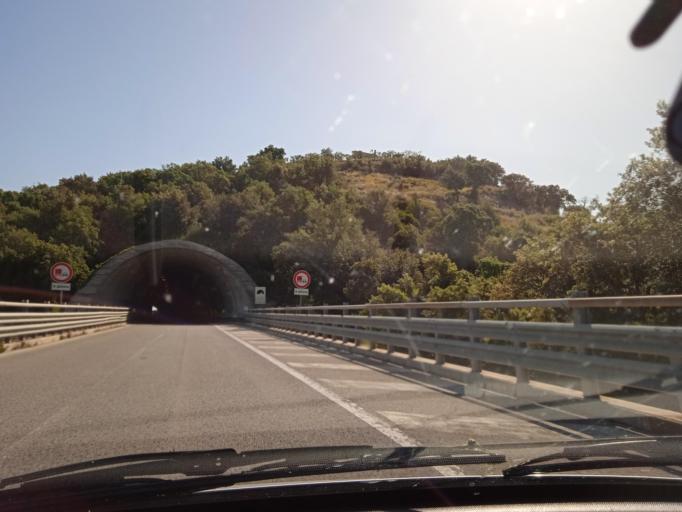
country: IT
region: Sicily
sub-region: Messina
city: Acquedolci
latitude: 38.0410
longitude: 14.5436
